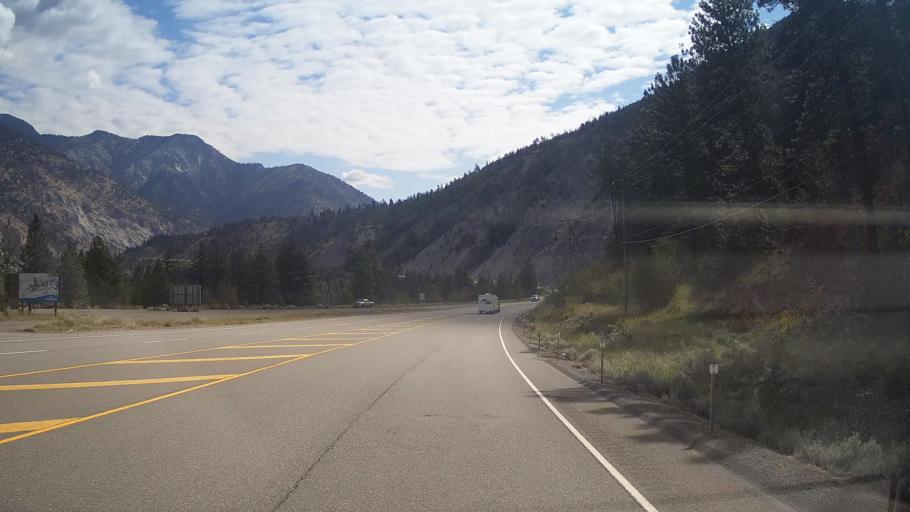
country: CA
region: British Columbia
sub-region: Thompson-Nicola Regional District
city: Ashcroft
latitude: 50.2492
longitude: -121.5621
